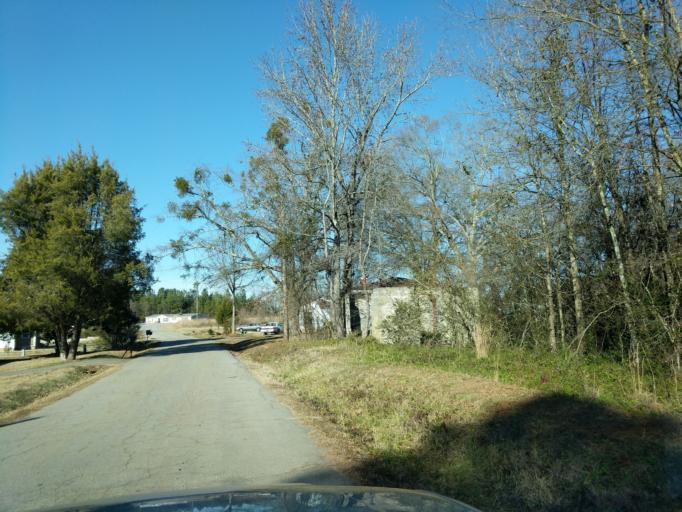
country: US
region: South Carolina
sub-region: Anderson County
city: Homeland Park
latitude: 34.4440
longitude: -82.7016
